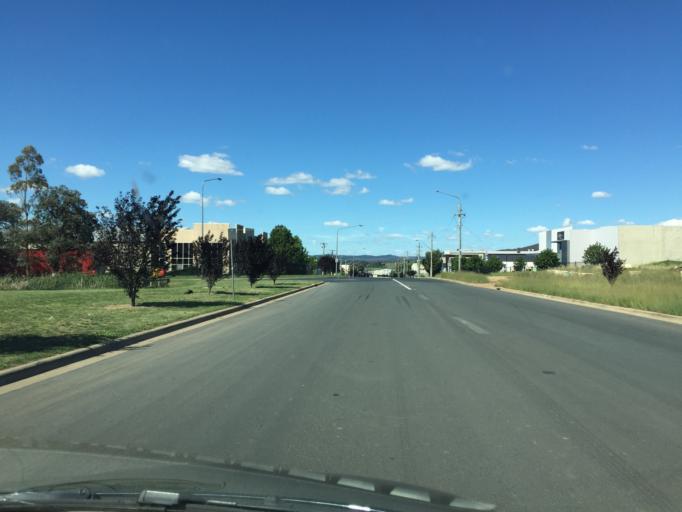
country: AU
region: Australian Capital Territory
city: Macarthur
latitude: -35.3943
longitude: 149.1624
